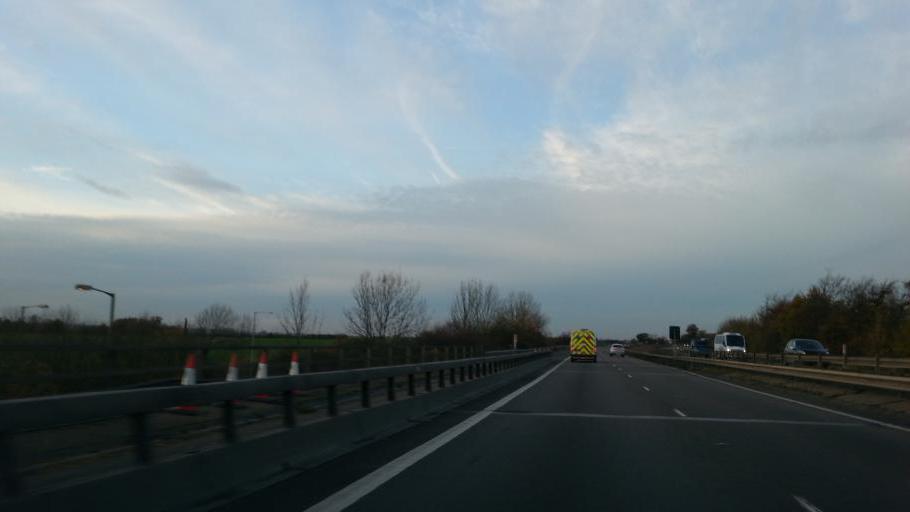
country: GB
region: England
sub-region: Central Bedfordshire
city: Stotfold
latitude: 52.0128
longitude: -0.2048
